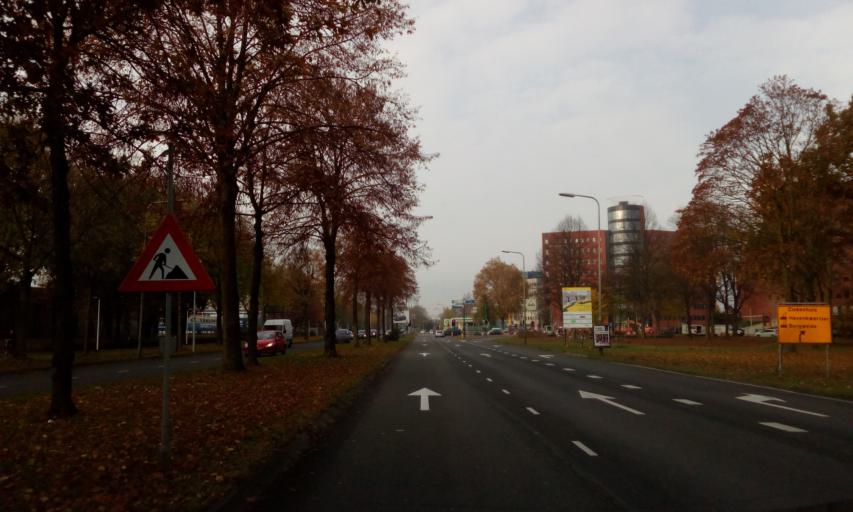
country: NL
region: Overijssel
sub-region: Gemeente Deventer
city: Deventer
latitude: 52.2406
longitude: 6.1749
